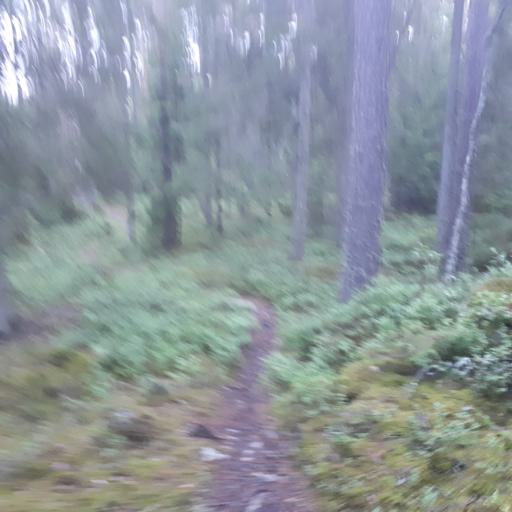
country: SE
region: Soedermanland
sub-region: Flens Kommun
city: Halleforsnas
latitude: 59.0858
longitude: 16.3942
